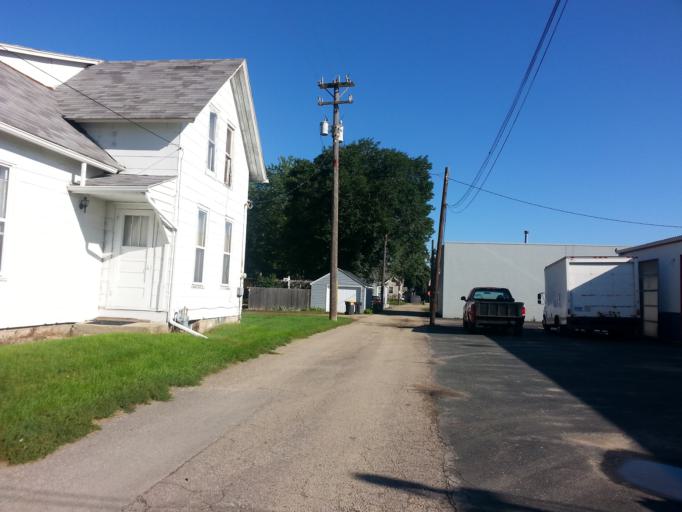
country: US
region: Minnesota
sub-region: Olmsted County
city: Rochester
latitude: 44.0351
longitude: -92.4637
